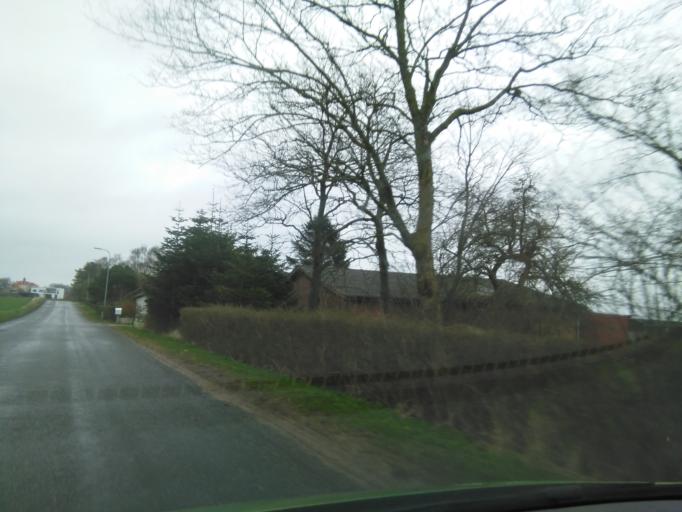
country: DK
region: Central Jutland
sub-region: Arhus Kommune
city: Kolt
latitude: 56.1484
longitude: 10.0618
